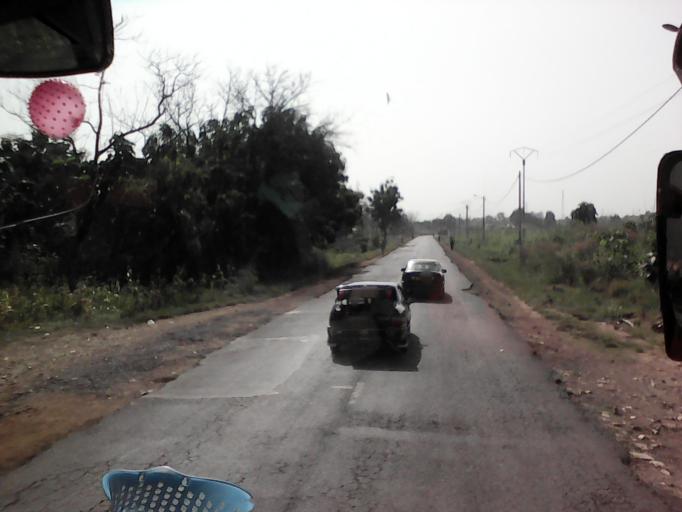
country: TG
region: Centrale
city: Sokode
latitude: 9.0281
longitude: 1.1376
